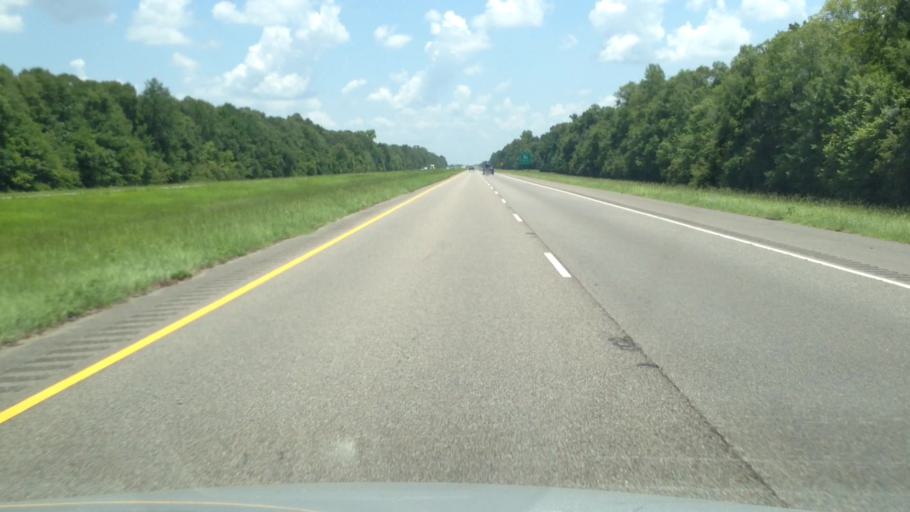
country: US
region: Louisiana
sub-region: Avoyelles Parish
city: Bunkie
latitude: 30.9709
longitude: -92.2920
